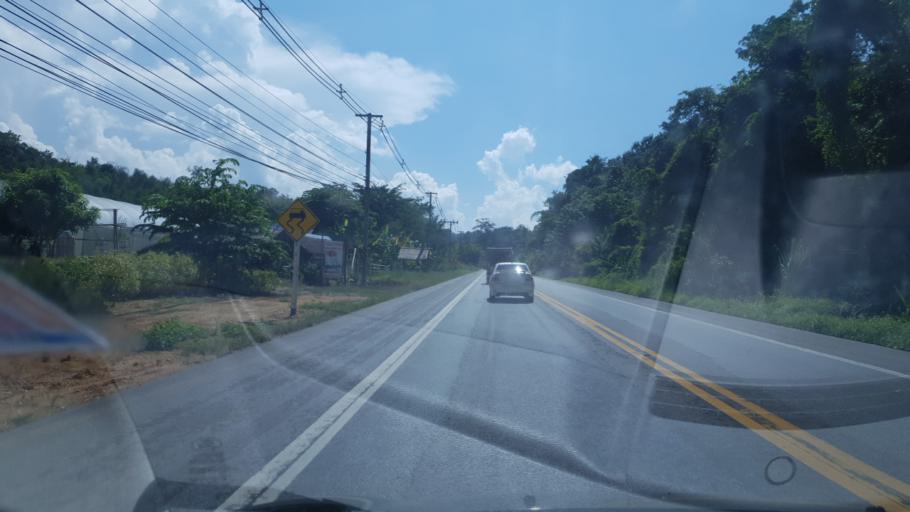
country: TH
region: Chiang Rai
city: Mae Suai
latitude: 19.6740
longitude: 99.5637
